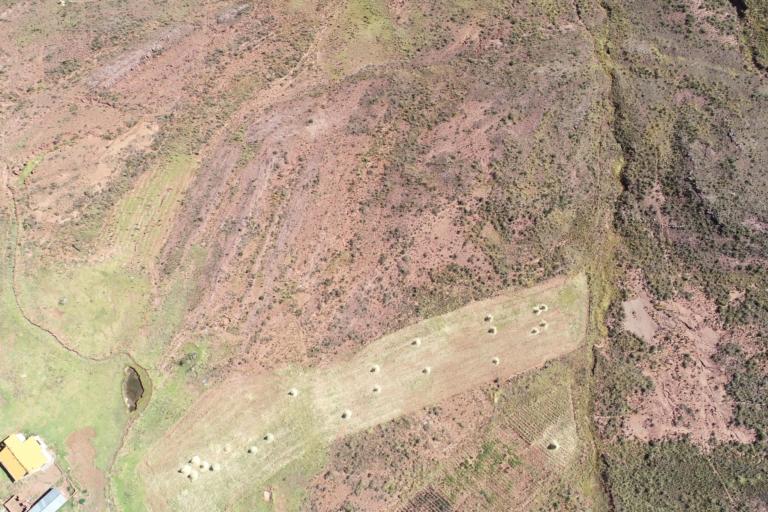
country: BO
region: La Paz
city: Tiahuanaco
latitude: -16.5992
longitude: -68.7593
